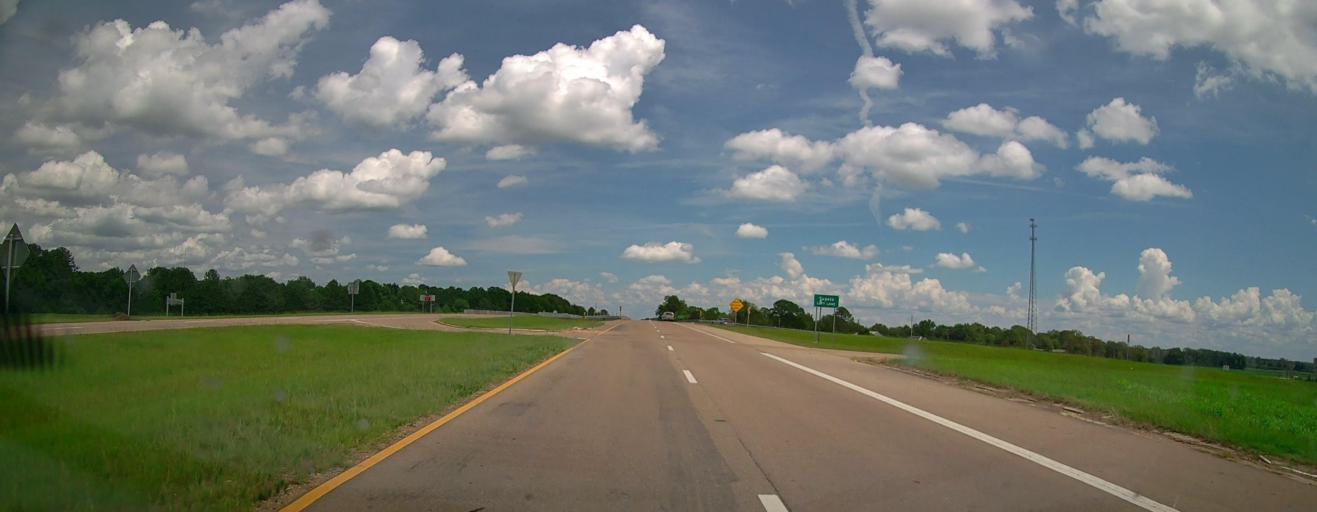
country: US
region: Mississippi
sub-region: Lee County
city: Shannon
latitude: 34.1177
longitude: -88.7036
